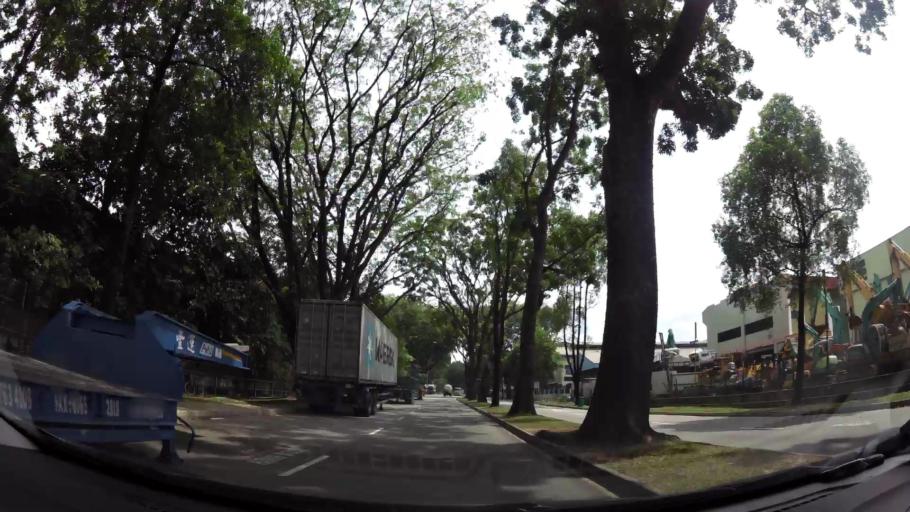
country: MY
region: Johor
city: Johor Bahru
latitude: 1.4171
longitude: 103.7436
